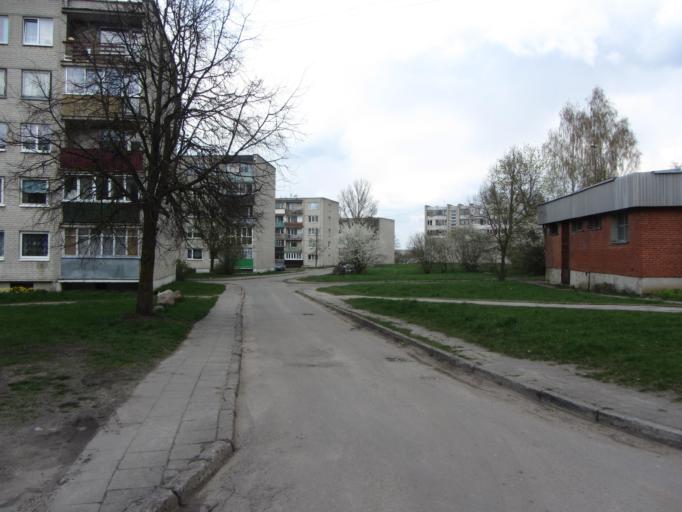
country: LT
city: Lentvaris
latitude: 54.6527
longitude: 25.0439
